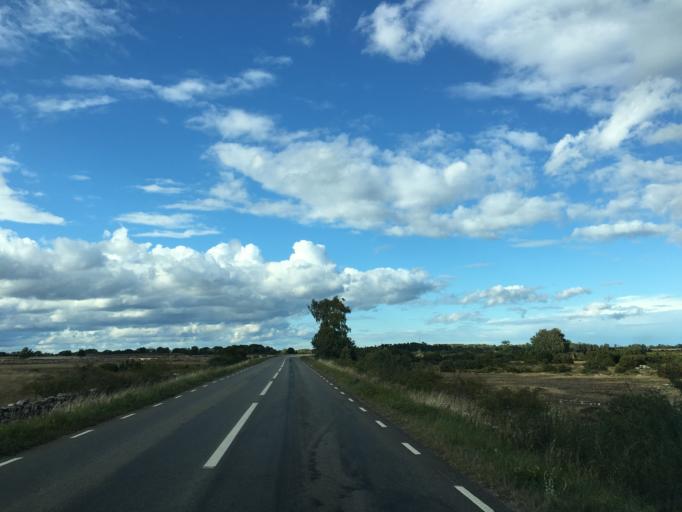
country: SE
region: Kalmar
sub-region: Morbylanga Kommun
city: Moerbylanga
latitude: 56.4966
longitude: 16.4262
